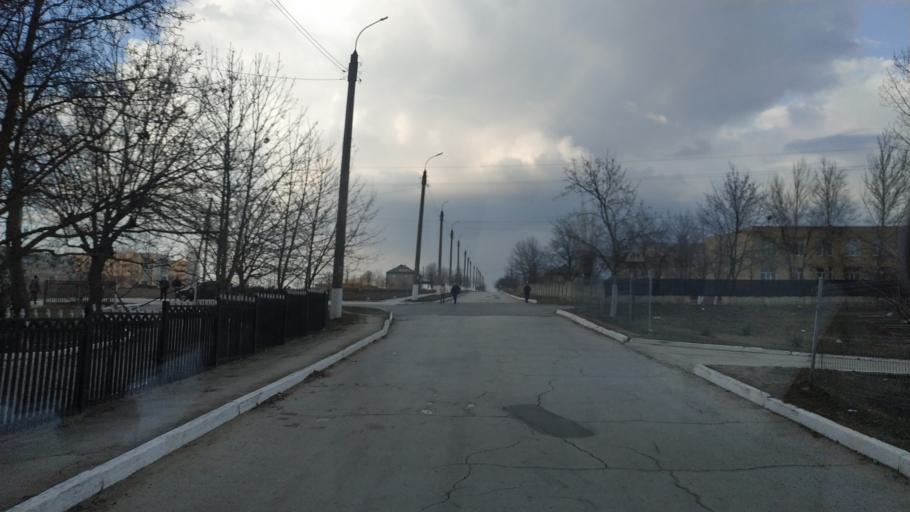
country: MD
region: Anenii Noi
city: Anenii Noi
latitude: 47.0095
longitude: 29.2948
